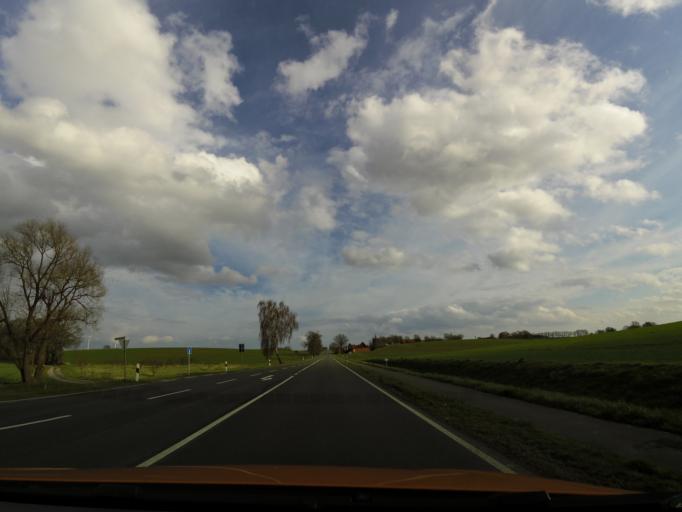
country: DE
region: Lower Saxony
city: Sustedt
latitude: 52.8333
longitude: 8.9195
